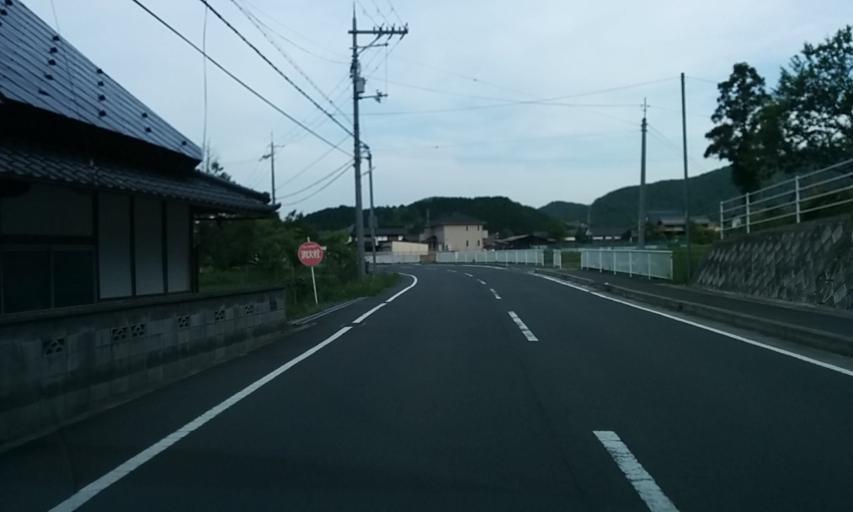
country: JP
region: Kyoto
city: Ayabe
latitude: 35.1704
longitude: 135.3831
